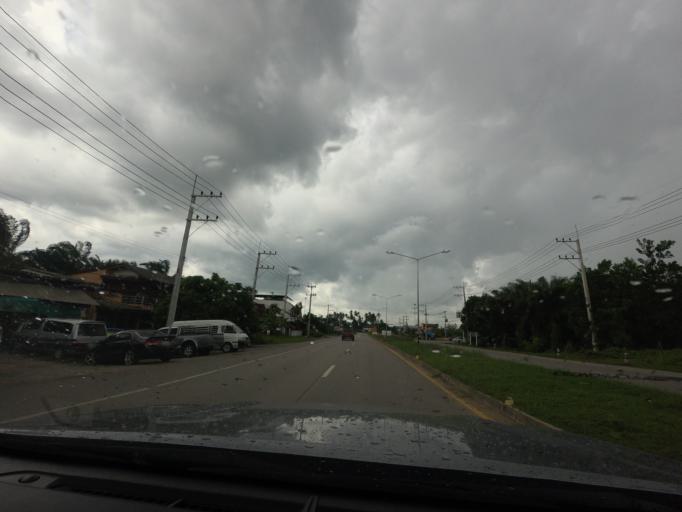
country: TH
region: Chumphon
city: Chumphon
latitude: 10.5005
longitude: 99.1631
